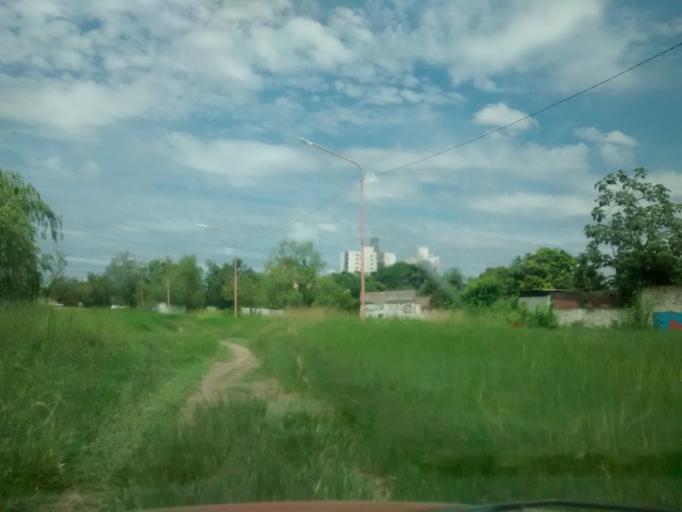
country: AR
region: Chaco
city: Resistencia
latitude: -27.4528
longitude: -58.9731
